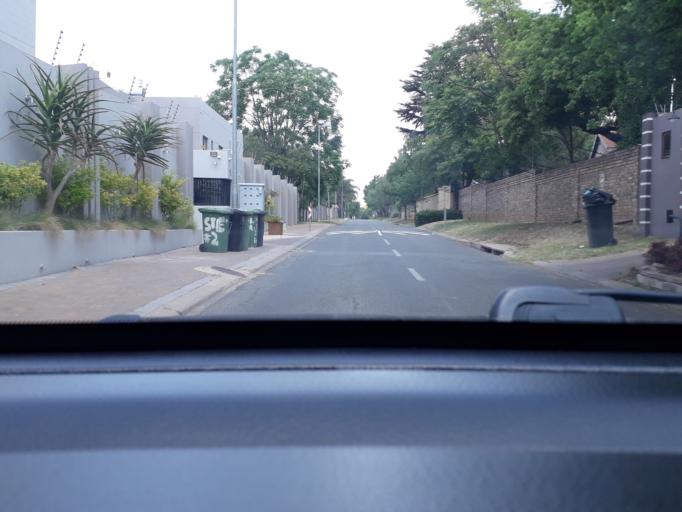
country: ZA
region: Gauteng
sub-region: City of Johannesburg Metropolitan Municipality
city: Midrand
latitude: -26.0550
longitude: 28.0631
